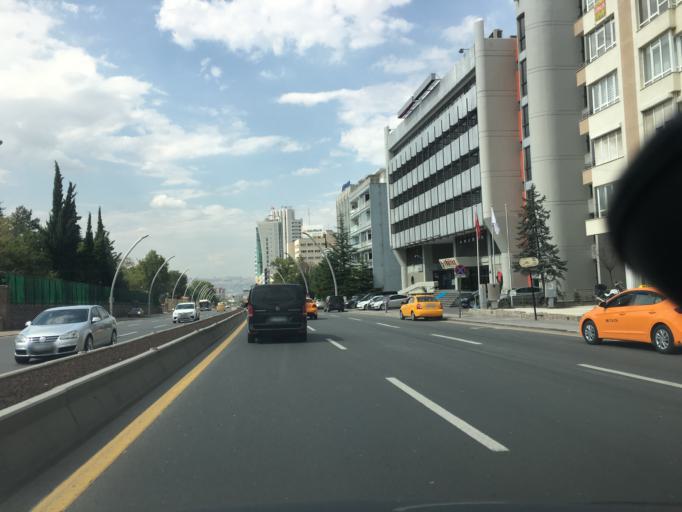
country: TR
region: Ankara
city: Cankaya
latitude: 39.9043
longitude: 32.8586
